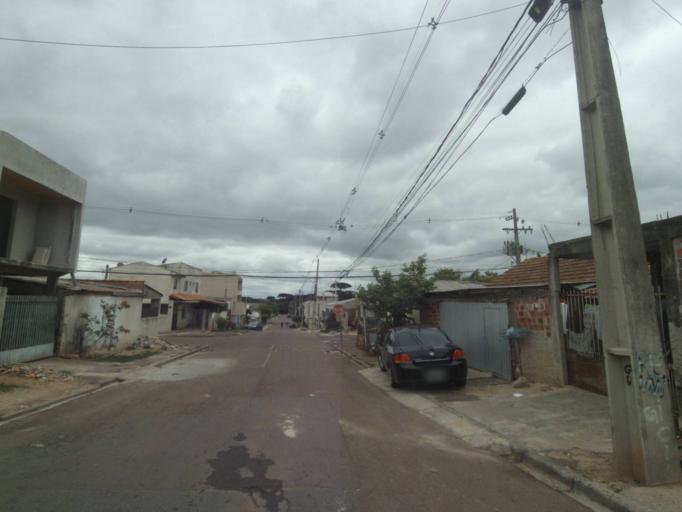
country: BR
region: Parana
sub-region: Sao Jose Dos Pinhais
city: Sao Jose dos Pinhais
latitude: -25.5578
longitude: -49.2644
